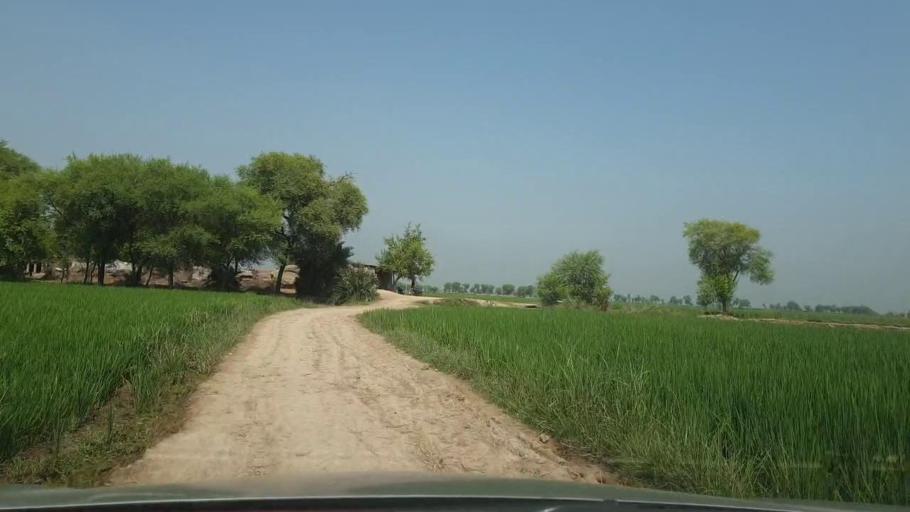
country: PK
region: Sindh
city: Kambar
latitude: 27.5941
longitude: 67.9071
